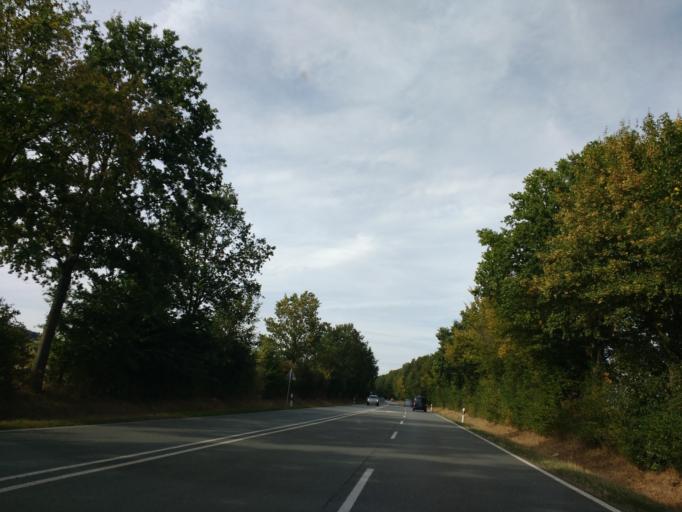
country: DE
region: North Rhine-Westphalia
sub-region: Regierungsbezirk Detmold
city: Nieheim
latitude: 51.7894
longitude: 9.1444
